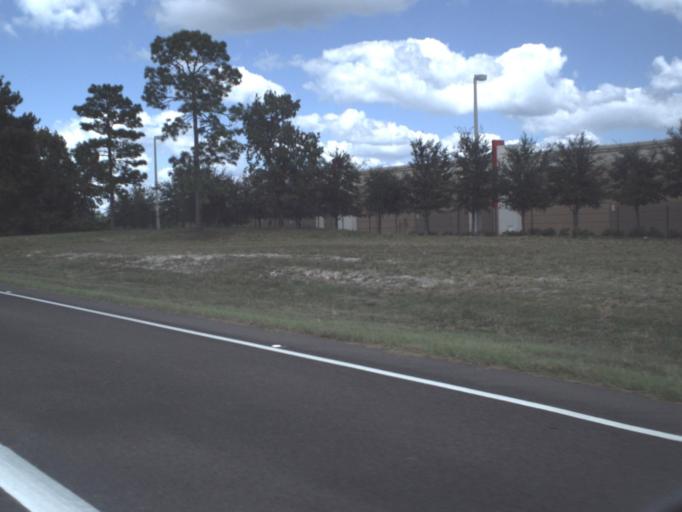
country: US
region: Florida
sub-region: Hernando County
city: Masaryktown
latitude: 28.4780
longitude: -82.4805
